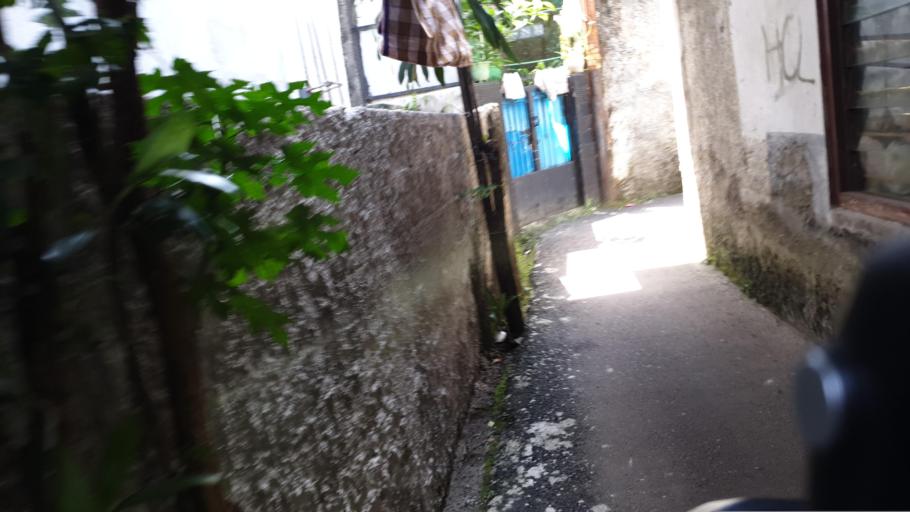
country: ID
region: Jakarta Raya
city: Jakarta
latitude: -6.2502
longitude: 106.7898
